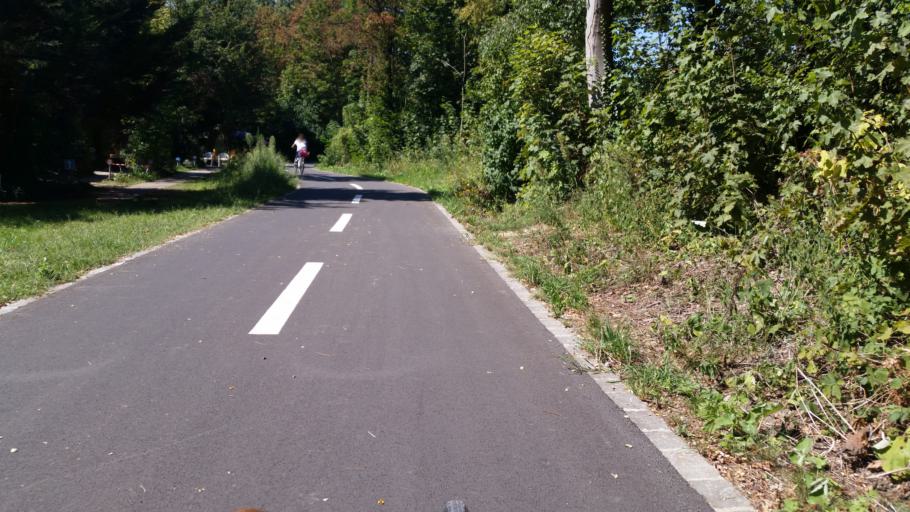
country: DE
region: Baden-Wuerttemberg
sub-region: Freiburg Region
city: Weil am Rhein
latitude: 47.5750
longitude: 7.6072
